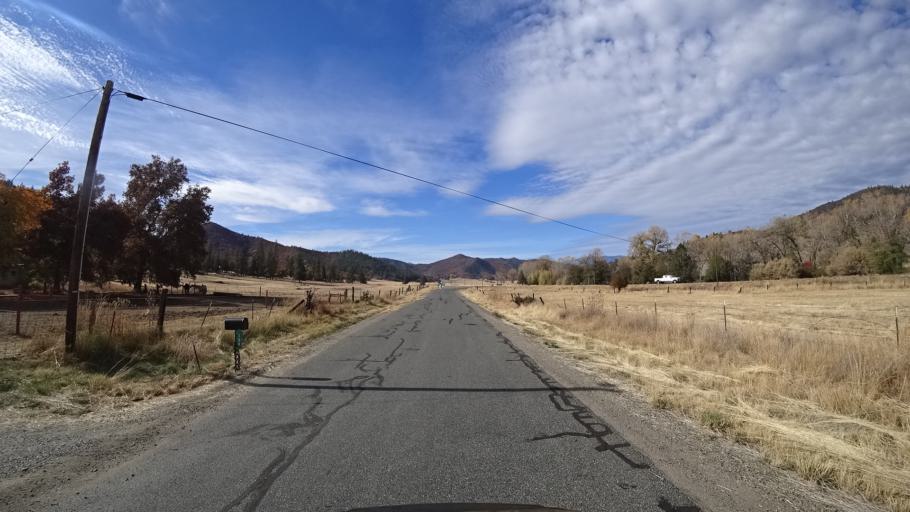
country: US
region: California
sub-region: Siskiyou County
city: Yreka
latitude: 41.6322
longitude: -122.7520
